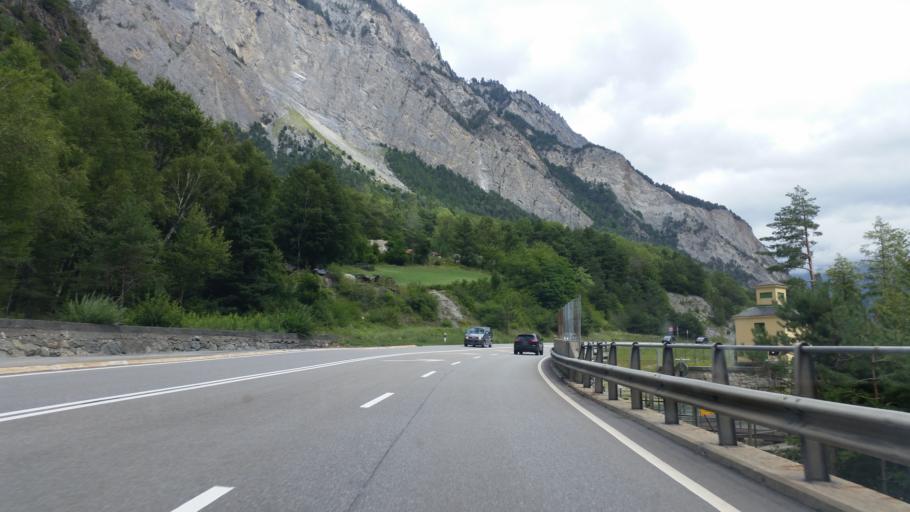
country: CH
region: Valais
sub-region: Martigny District
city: Charrat-les-Chenes
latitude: 46.0790
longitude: 7.1272
